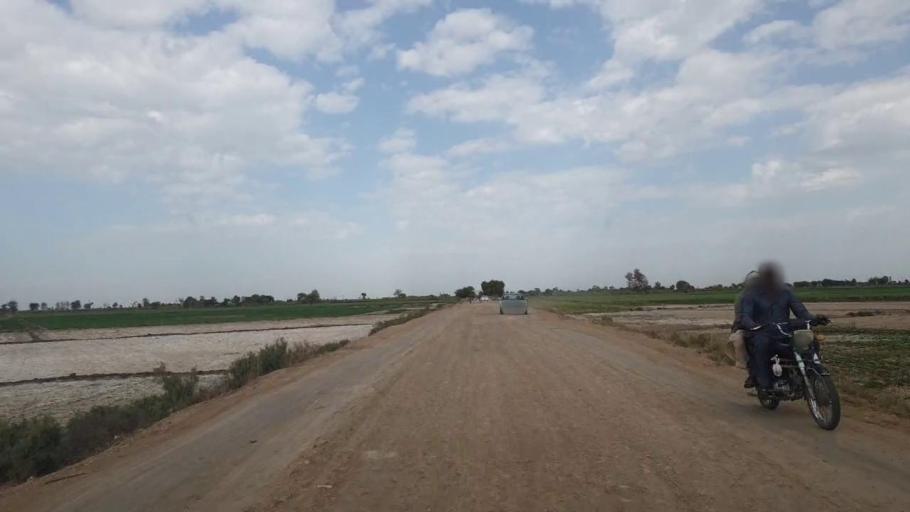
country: PK
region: Sindh
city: Hala
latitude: 25.9616
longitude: 68.4679
